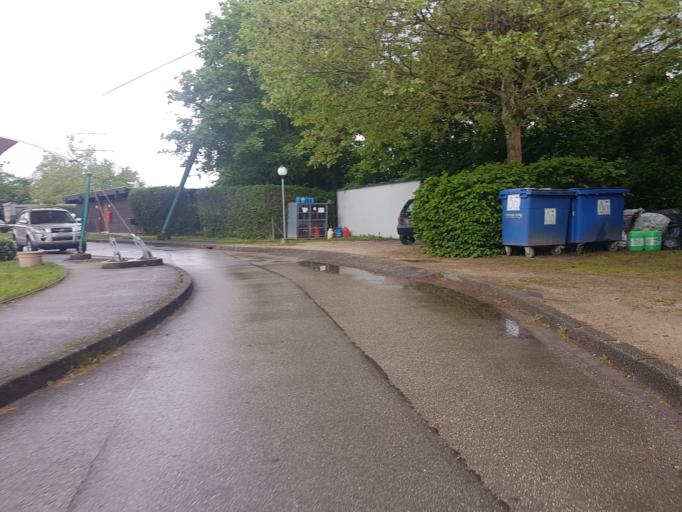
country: CH
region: Geneva
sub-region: Geneva
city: Vernier
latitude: 46.2014
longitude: 6.0669
